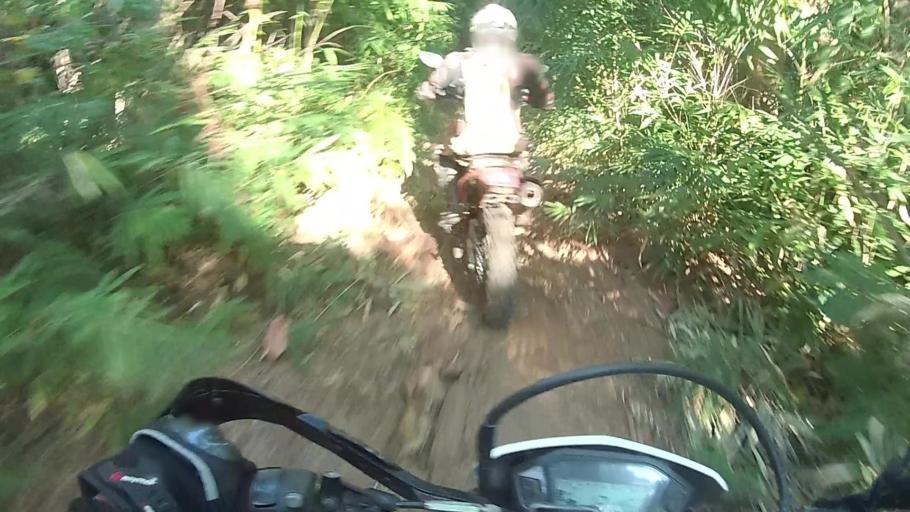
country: TH
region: Chiang Mai
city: Mae Taeng
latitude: 18.9571
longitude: 98.8785
